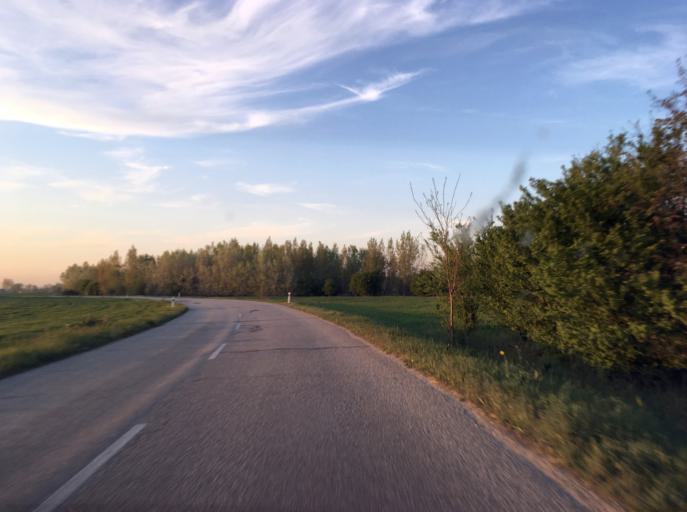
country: SK
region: Nitriansky
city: Kolarovo
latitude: 47.8853
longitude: 17.9244
